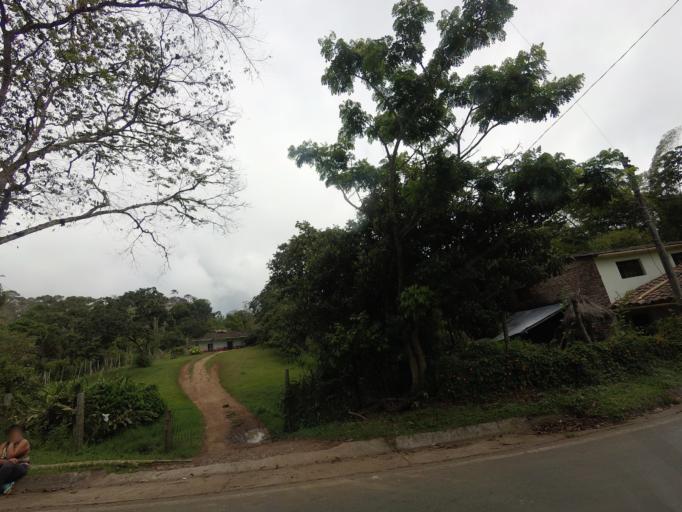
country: CO
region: Huila
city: San Agustin
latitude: 1.8873
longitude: -76.2804
